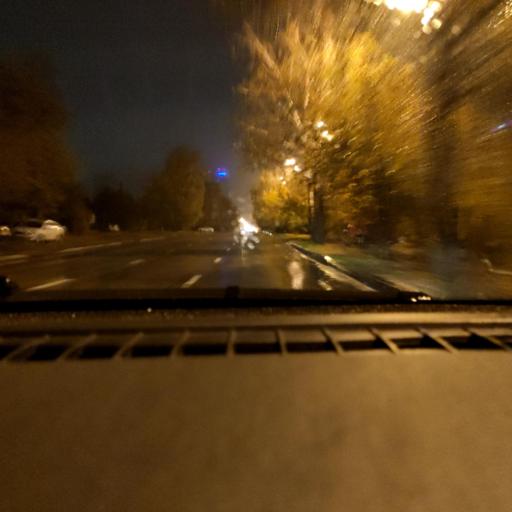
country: RU
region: Voronezj
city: Voronezh
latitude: 51.6949
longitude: 39.1754
